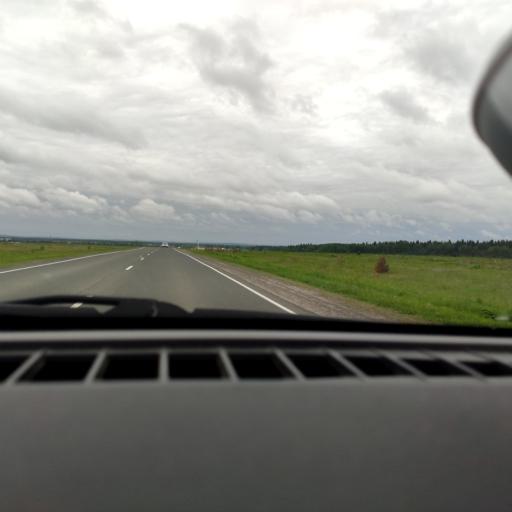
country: RU
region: Perm
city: Ust'-Kachka
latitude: 57.9646
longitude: 55.7281
